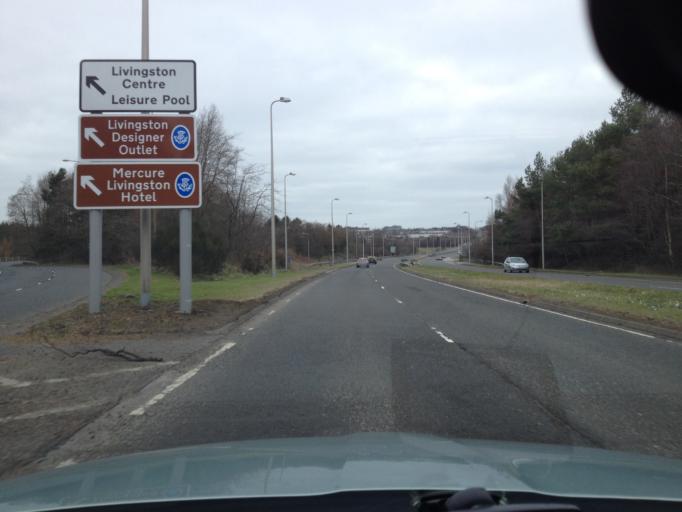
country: GB
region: Scotland
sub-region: West Lothian
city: Mid Calder
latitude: 55.8855
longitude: -3.4988
